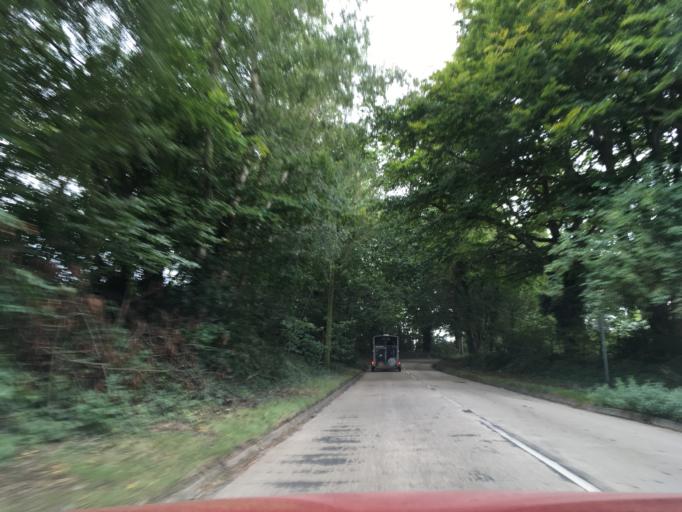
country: GB
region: England
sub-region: Kent
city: Yalding
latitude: 51.2371
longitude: 0.4469
